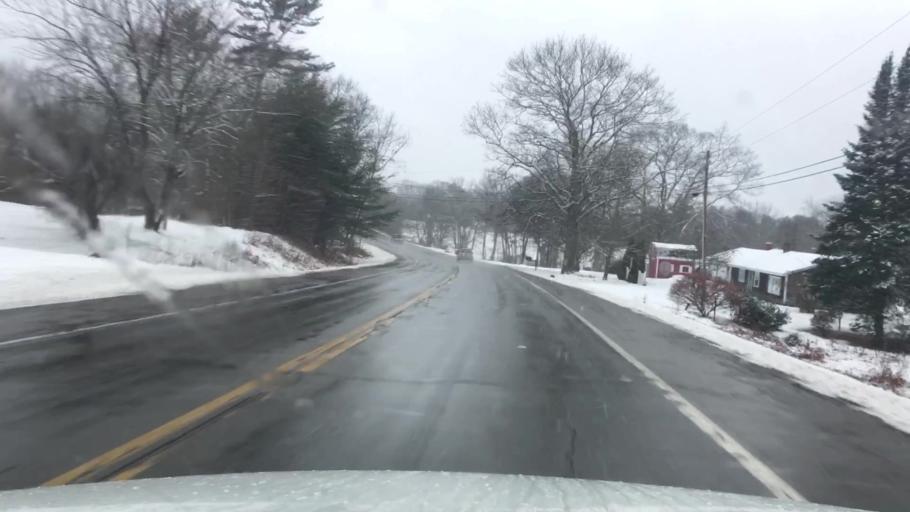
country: US
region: Maine
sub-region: Knox County
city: Warren
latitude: 44.1359
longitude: -69.2235
